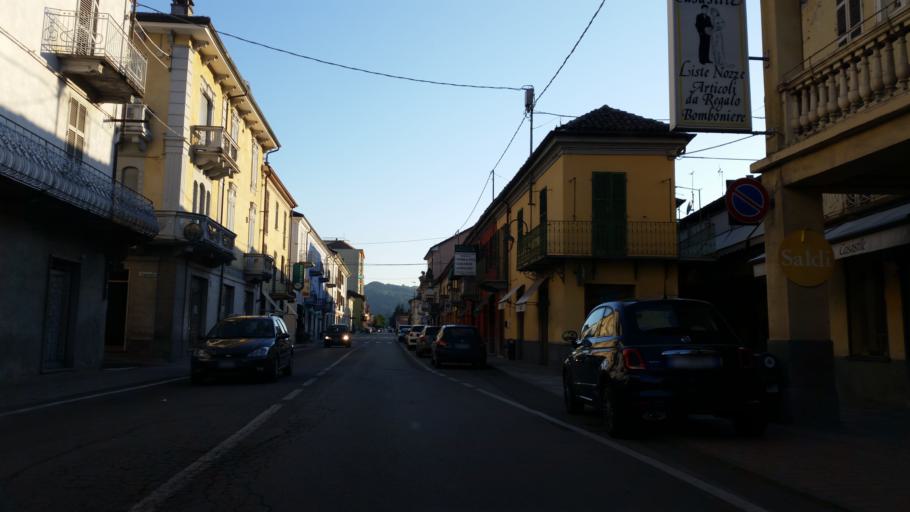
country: IT
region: Piedmont
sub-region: Provincia di Cuneo
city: Santo Stefano Belbo
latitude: 44.7079
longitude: 8.2294
